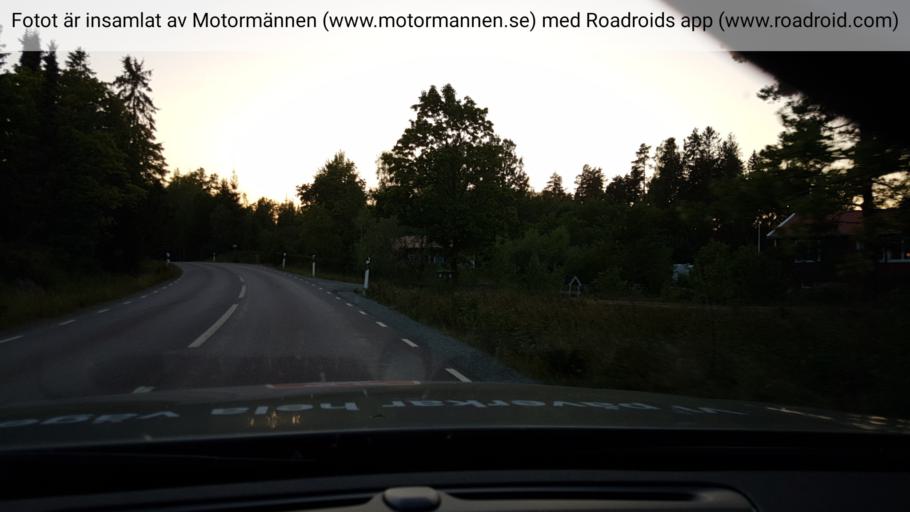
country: SE
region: Uppsala
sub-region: Heby Kommun
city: OEstervala
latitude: 60.0334
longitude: 17.2686
